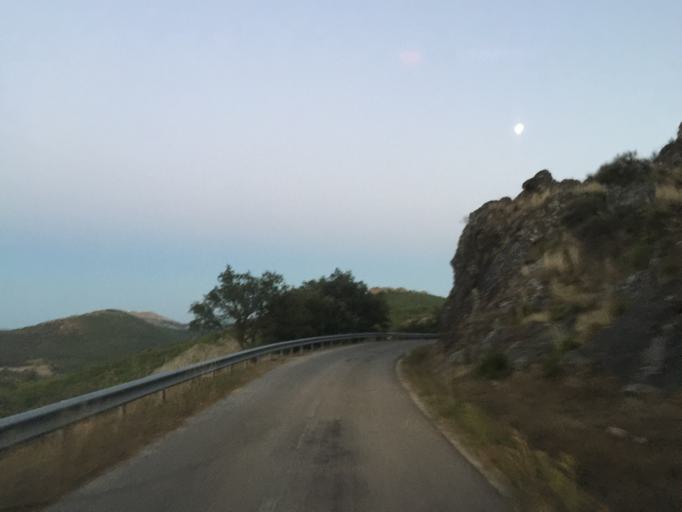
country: PT
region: Portalegre
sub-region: Castelo de Vide
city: Castelo de Vide
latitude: 39.4035
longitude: -7.4548
